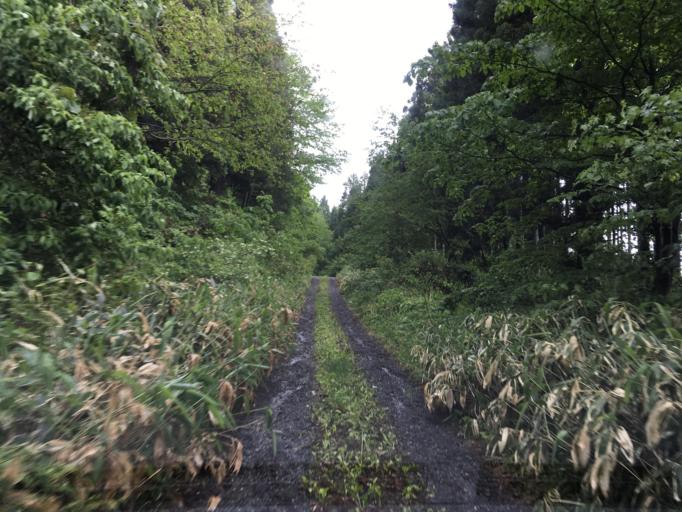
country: JP
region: Iwate
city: Ichinoseki
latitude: 38.8679
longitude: 141.4450
